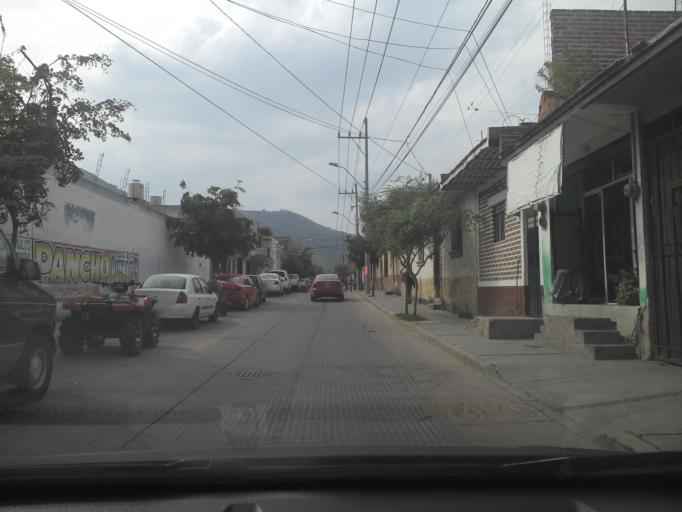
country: MX
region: Jalisco
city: Tlajomulco de Zuniga
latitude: 20.4775
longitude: -103.4467
